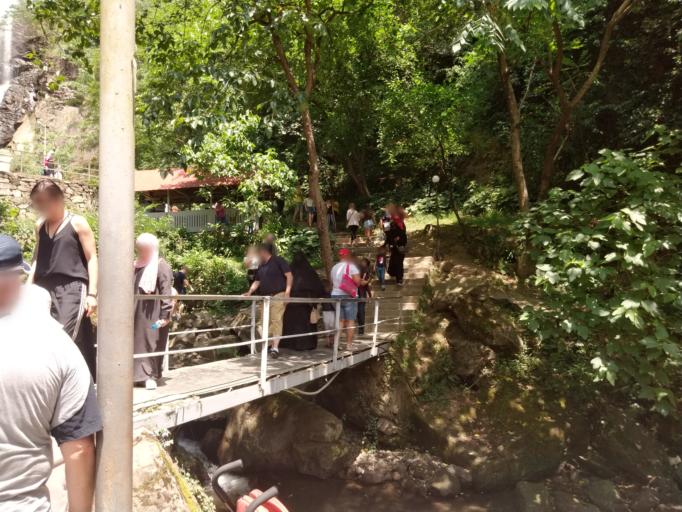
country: GE
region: Ajaria
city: Keda
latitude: 41.5744
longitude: 41.8588
